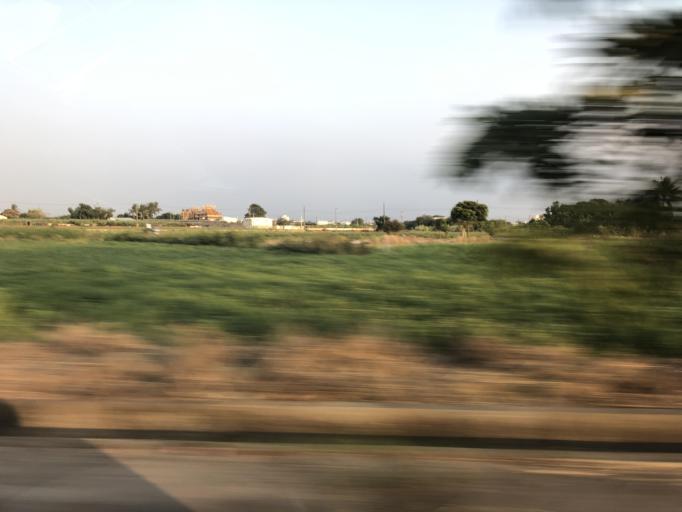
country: TW
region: Taiwan
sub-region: Tainan
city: Tainan
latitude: 23.1383
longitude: 120.2649
